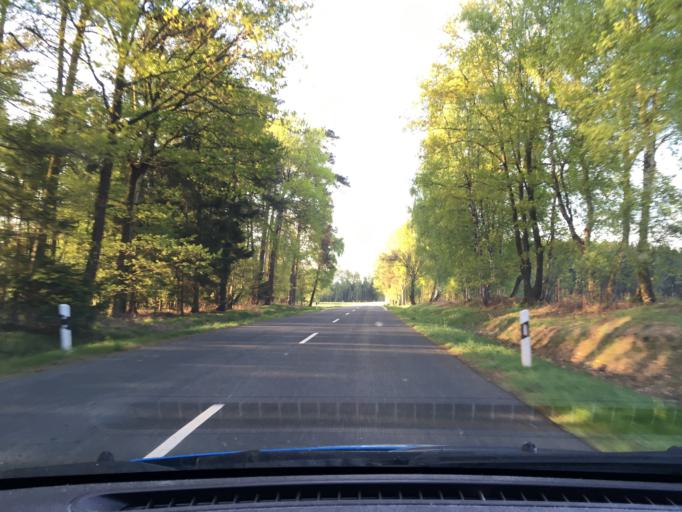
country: DE
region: Lower Saxony
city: Bispingen
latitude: 53.0056
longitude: 9.9965
